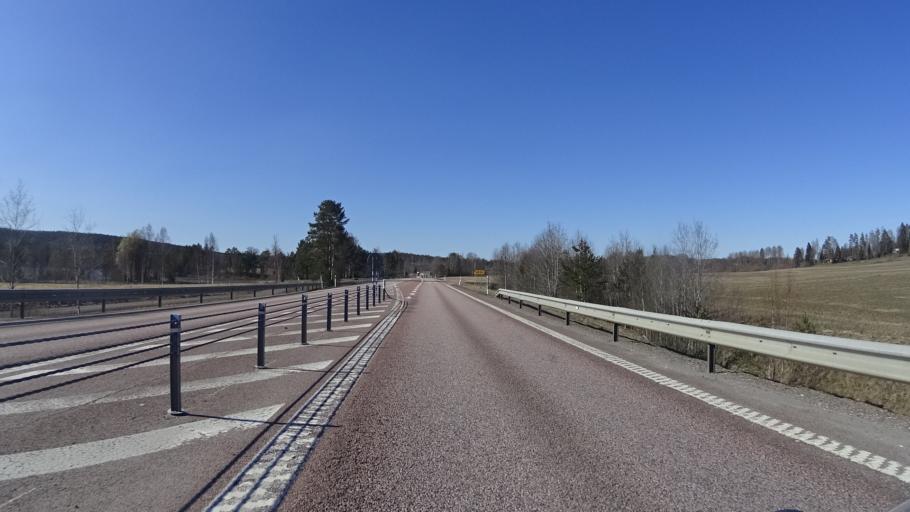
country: SE
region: Vaermland
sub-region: Karlstads Kommun
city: Edsvalla
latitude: 59.5152
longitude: 13.1716
